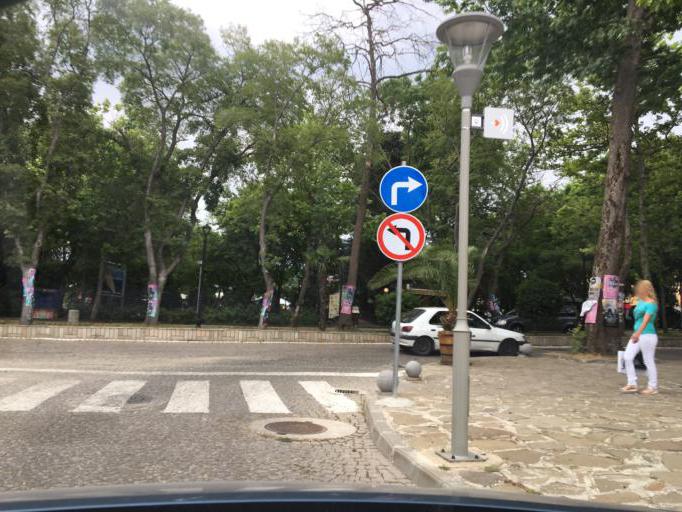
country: BG
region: Burgas
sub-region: Obshtina Sozopol
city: Sozopol
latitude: 42.4199
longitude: 27.6932
